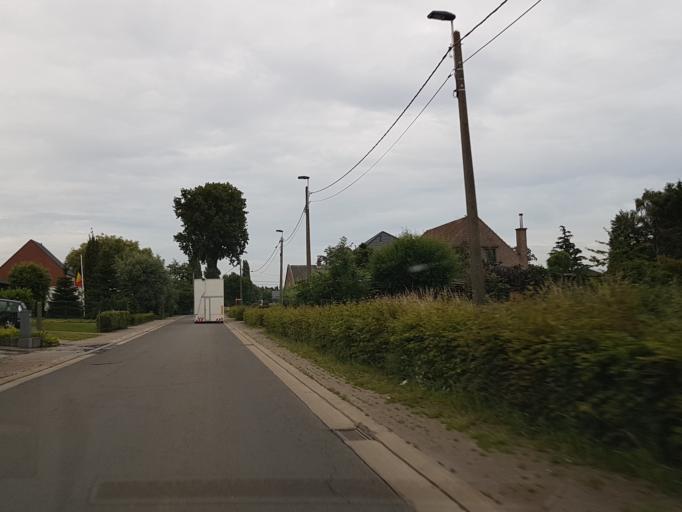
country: BE
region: Flanders
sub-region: Provincie Vlaams-Brabant
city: Londerzeel
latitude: 50.9979
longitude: 4.3280
